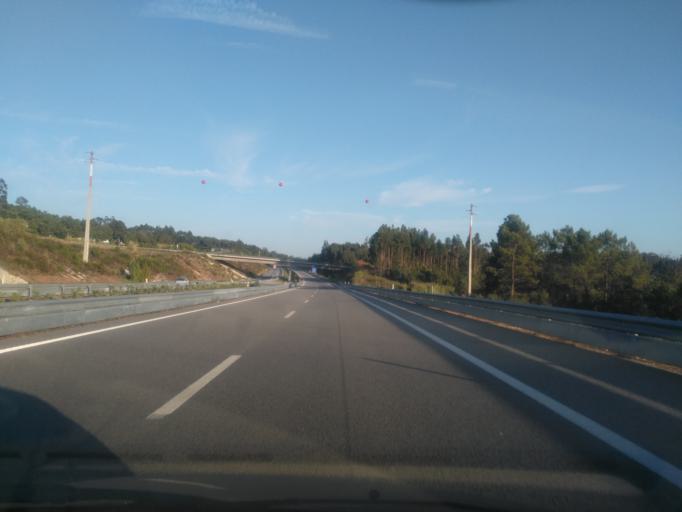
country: PT
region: Coimbra
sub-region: Figueira da Foz
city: Alhadas
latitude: 40.1775
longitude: -8.8014
